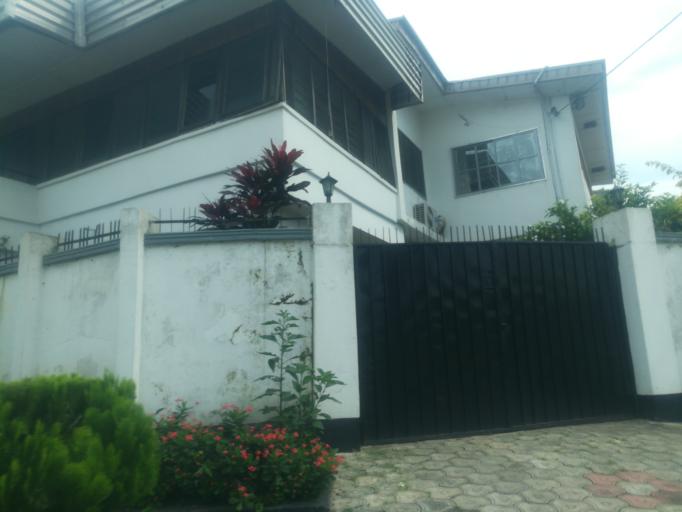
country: NG
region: Oyo
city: Ibadan
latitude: 7.4245
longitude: 3.9122
